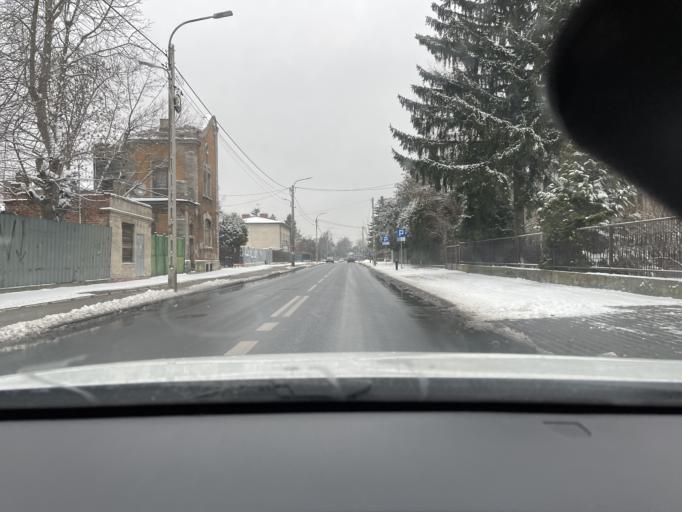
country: PL
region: Masovian Voivodeship
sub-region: Powiat zyrardowski
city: Zyrardow
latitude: 52.0549
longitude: 20.4527
